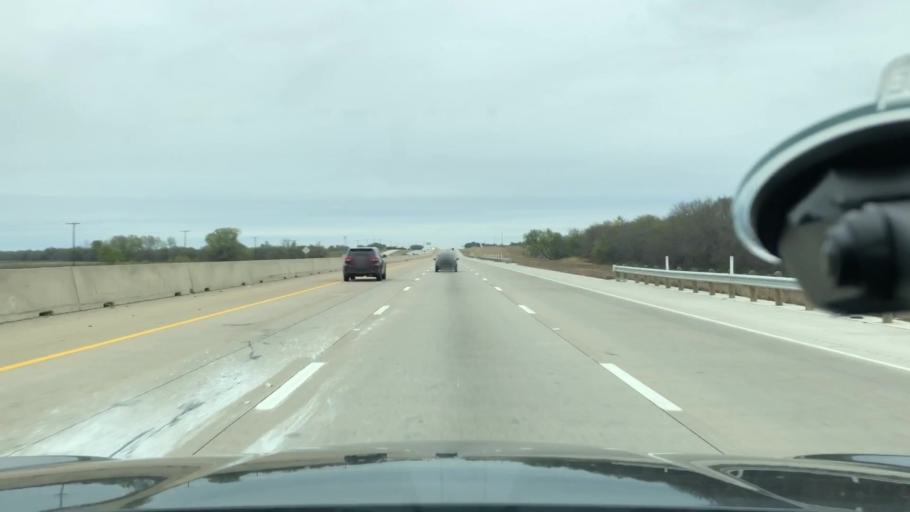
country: US
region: Texas
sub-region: Ellis County
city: Nash
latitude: 32.2670
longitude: -96.8714
